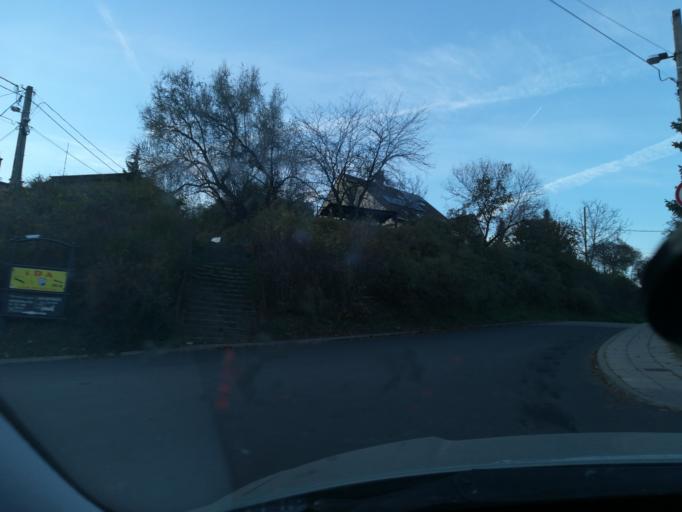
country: HU
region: Budapest
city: Budapest XI. keruelet
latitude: 47.4800
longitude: 19.0235
